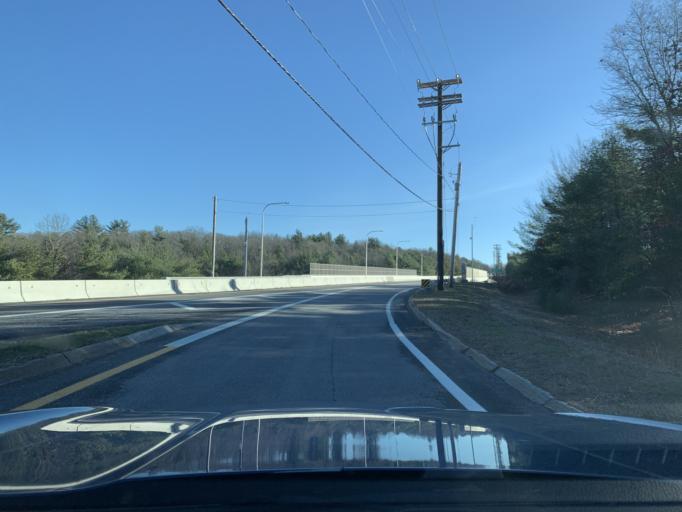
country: US
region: Rhode Island
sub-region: Kent County
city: West Greenwich
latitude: 41.6041
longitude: -71.6586
